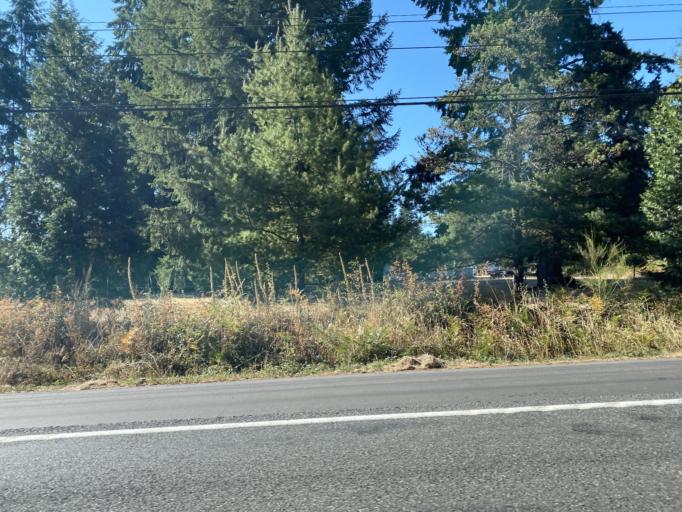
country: US
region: Washington
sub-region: Thurston County
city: Tanglewilde-Thompson Place
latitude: 46.9855
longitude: -122.7470
